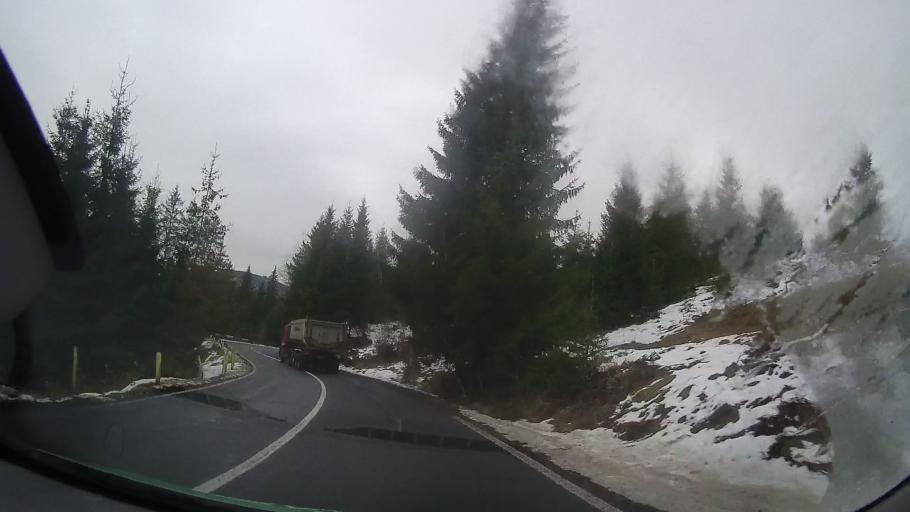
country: RO
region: Harghita
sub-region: Municipiul Gheorgheni
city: Gheorgheni
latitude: 46.7744
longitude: 25.6997
